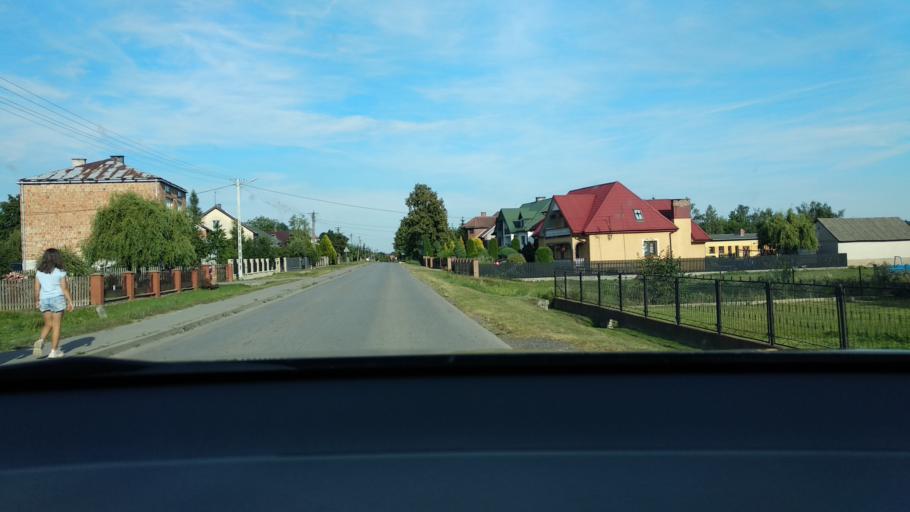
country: PL
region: Masovian Voivodeship
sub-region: Powiat pultuski
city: Obryte
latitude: 52.7140
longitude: 21.1869
